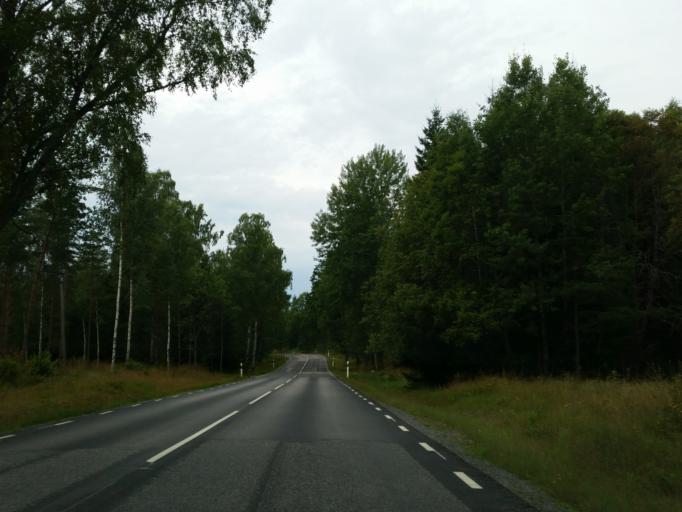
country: SE
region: Stockholm
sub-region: Nykvarns Kommun
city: Nykvarn
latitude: 59.1894
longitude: 17.5094
